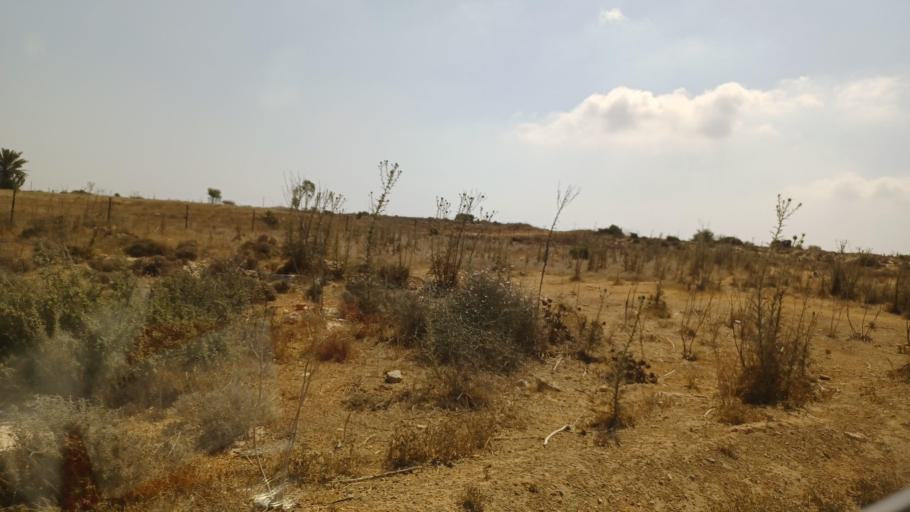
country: CY
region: Ammochostos
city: Frenaros
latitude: 35.0673
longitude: 33.9242
